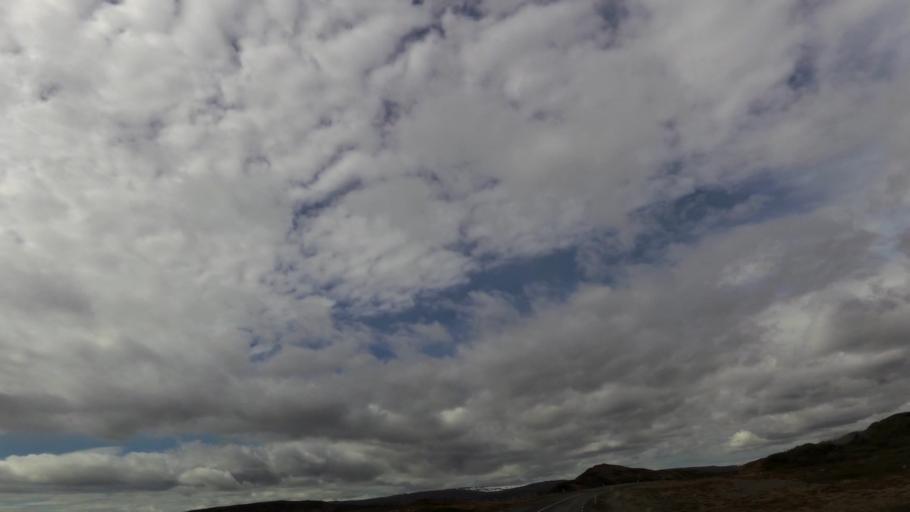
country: IS
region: West
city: Stykkisholmur
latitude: 65.5366
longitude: -22.0952
